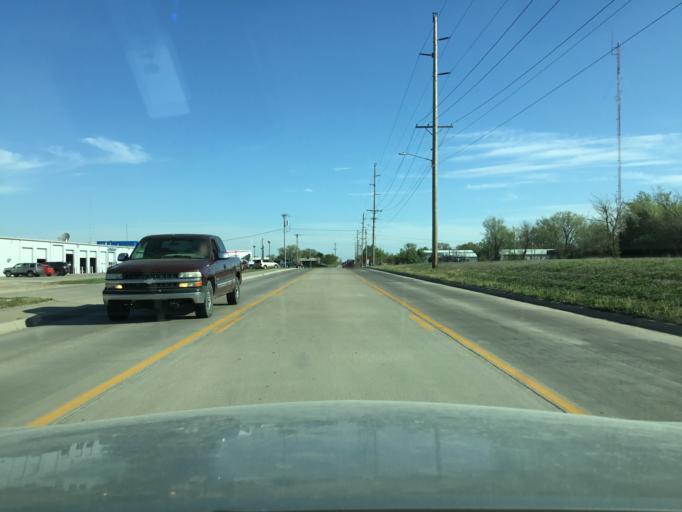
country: US
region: Kansas
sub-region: Neosho County
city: Chanute
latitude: 37.6872
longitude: -95.4710
